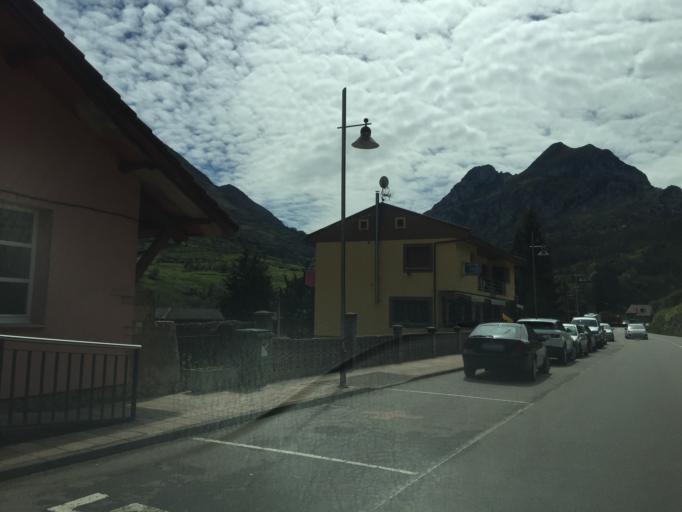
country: ES
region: Asturias
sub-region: Province of Asturias
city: Proaza
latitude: 43.2551
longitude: -6.0139
